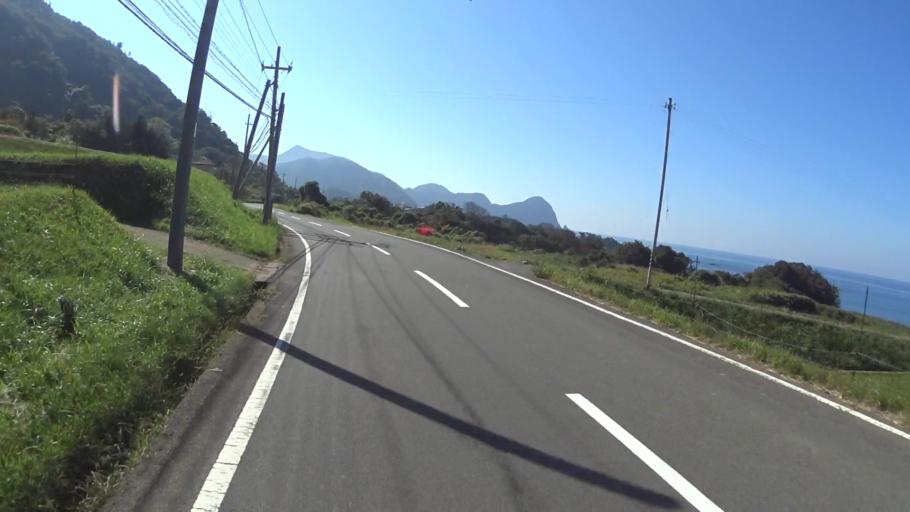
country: JP
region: Kyoto
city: Miyazu
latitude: 35.7636
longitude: 135.1876
